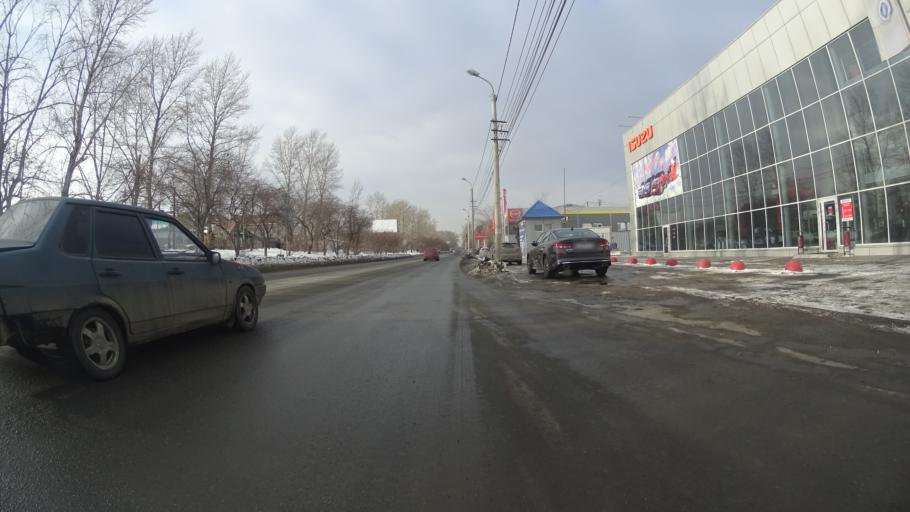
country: RU
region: Chelyabinsk
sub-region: Gorod Chelyabinsk
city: Chelyabinsk
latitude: 55.1191
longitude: 61.3828
